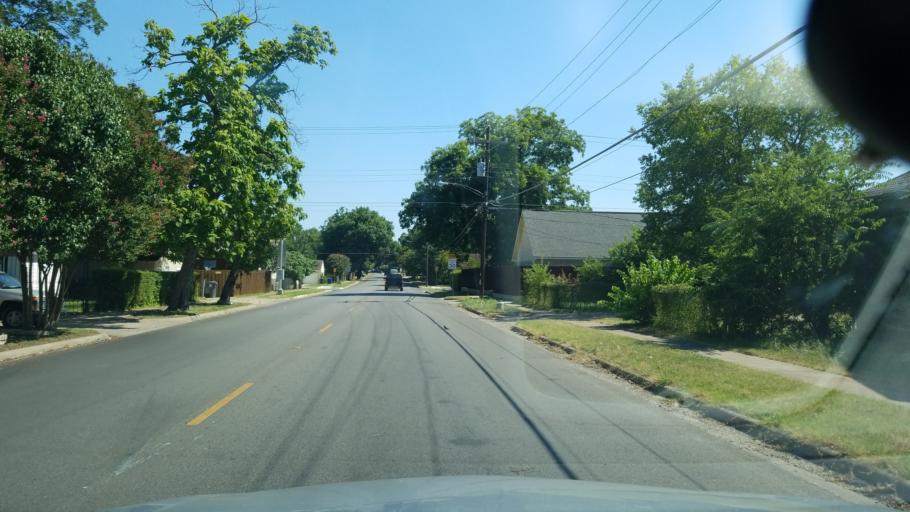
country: US
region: Texas
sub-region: Dallas County
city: Cockrell Hill
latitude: 32.7232
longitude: -96.8446
